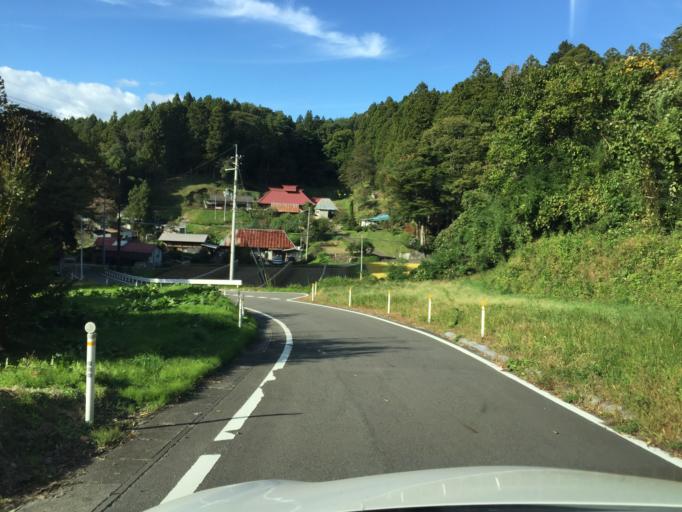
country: JP
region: Fukushima
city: Ishikawa
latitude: 37.1721
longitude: 140.4787
